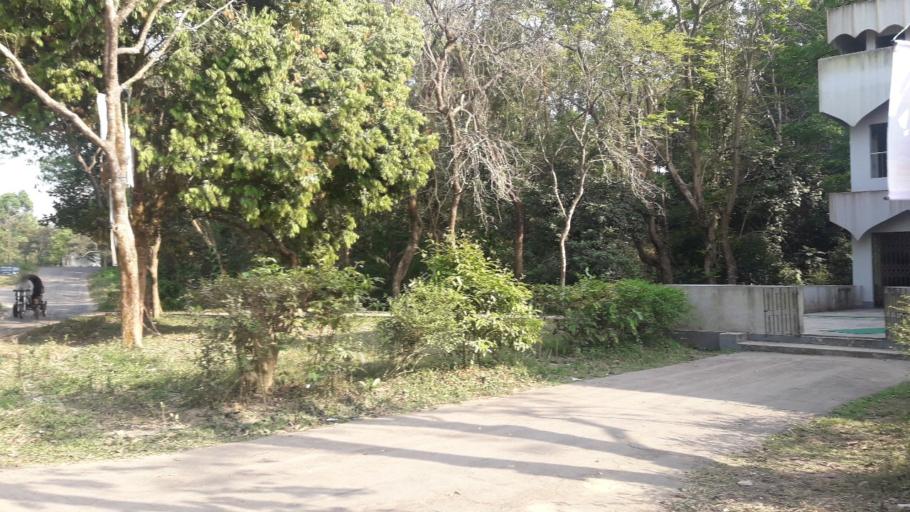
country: BD
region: Chittagong
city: Chittagong
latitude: 22.4678
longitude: 91.7941
